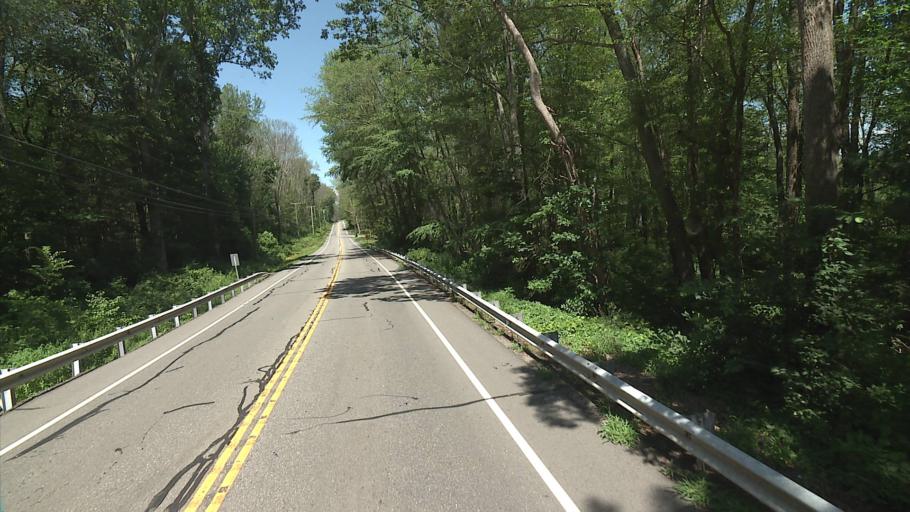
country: US
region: Connecticut
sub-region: Windham County
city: Plainfield Village
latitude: 41.7013
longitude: -72.0042
